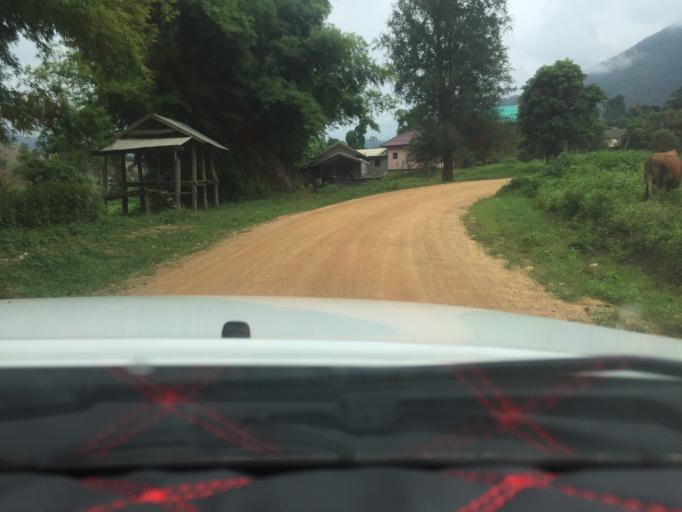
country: TH
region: Phayao
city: Phu Sang
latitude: 19.6833
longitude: 100.5017
